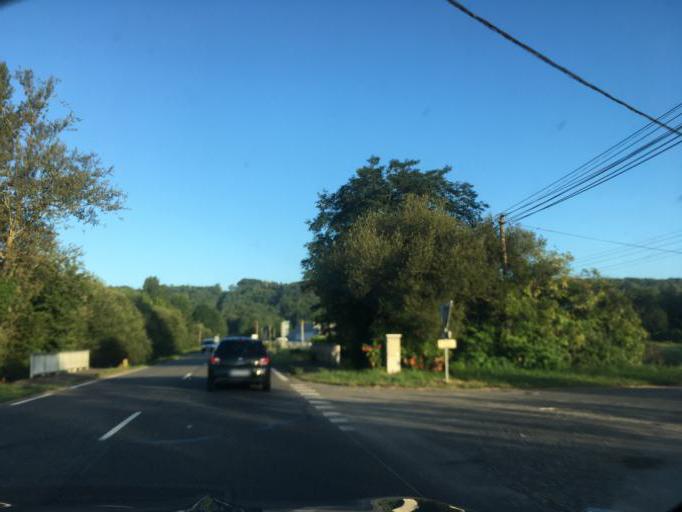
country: FR
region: Midi-Pyrenees
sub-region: Departement des Hautes-Pyrenees
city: Ibos
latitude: 43.2432
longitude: -0.0091
